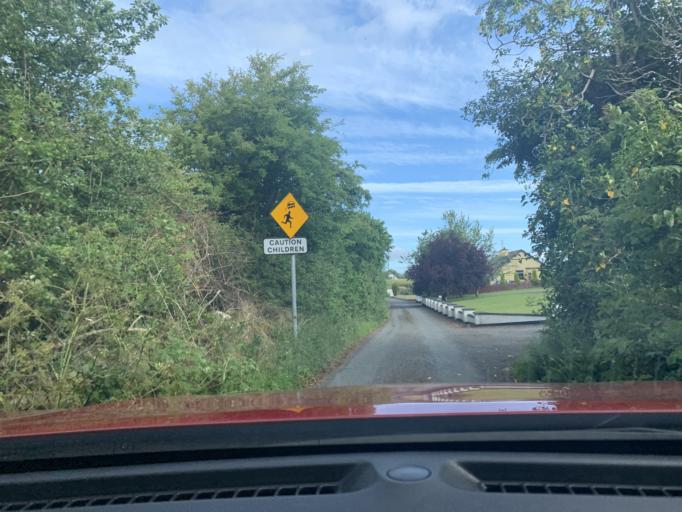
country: IE
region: Connaught
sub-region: Sligo
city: Sligo
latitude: 54.2330
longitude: -8.4666
